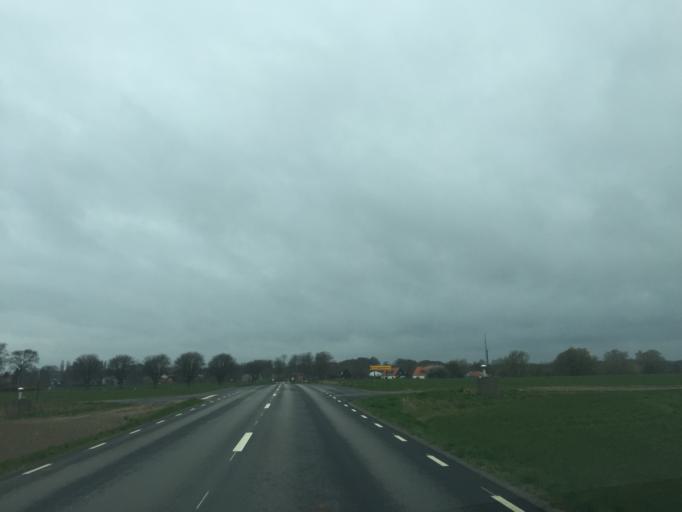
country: SE
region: Skane
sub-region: Skurups Kommun
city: Skivarp
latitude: 55.4250
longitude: 13.5902
